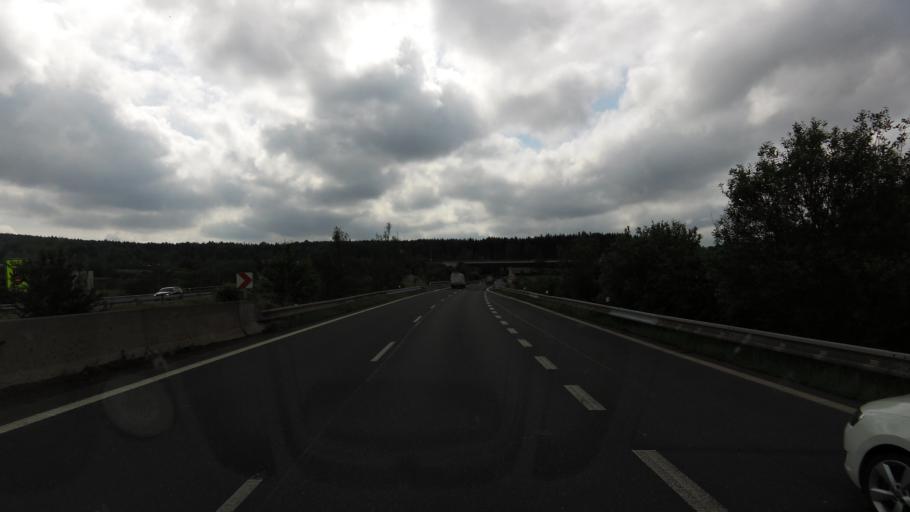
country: CZ
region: Plzensky
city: Dysina
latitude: 49.7381
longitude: 13.5069
